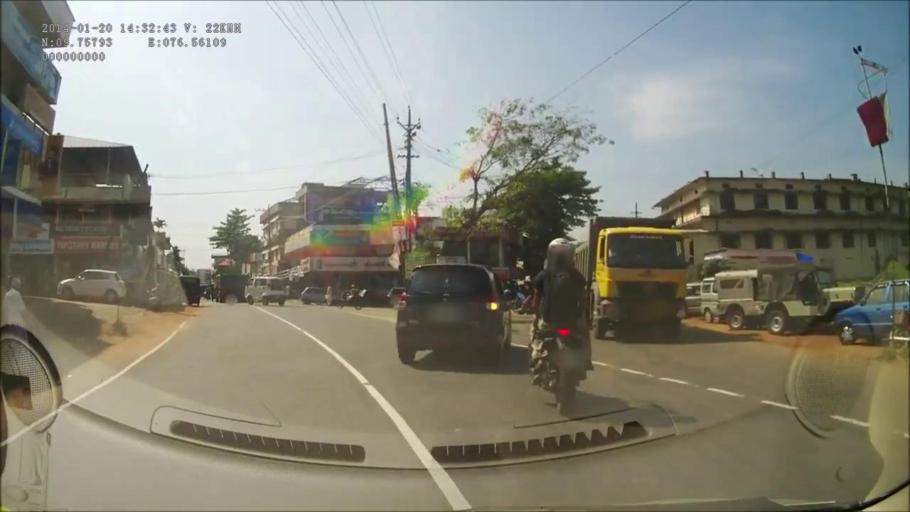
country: IN
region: Kerala
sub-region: Kottayam
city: Palackattumala
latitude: 9.7576
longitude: 76.5606
